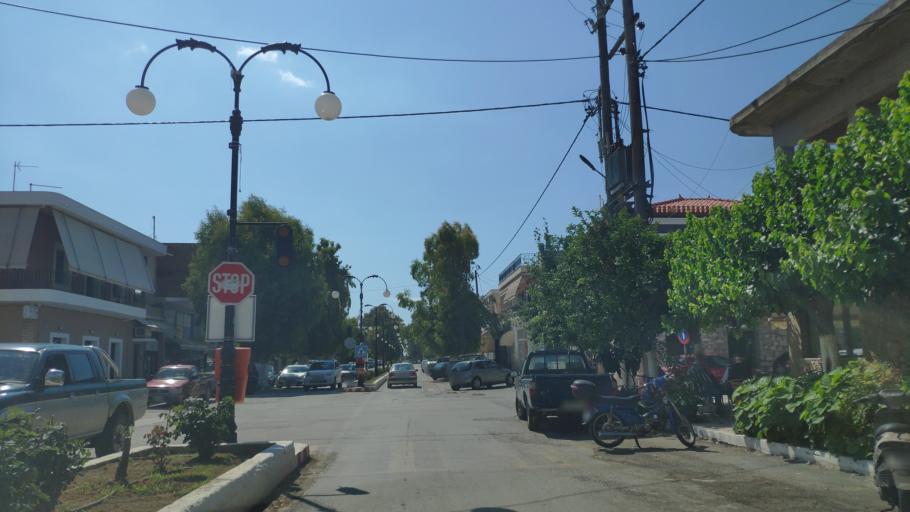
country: GR
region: Central Greece
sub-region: Nomos Evvoias
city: Eretria
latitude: 38.3939
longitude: 23.7929
